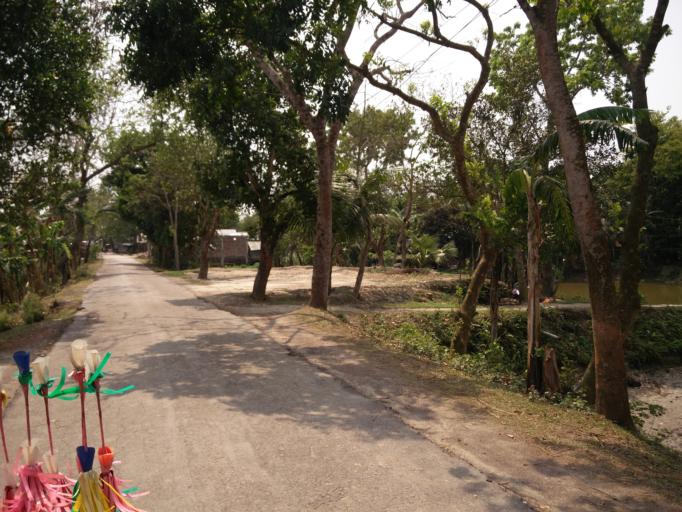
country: BD
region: Dhaka
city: Sherpur
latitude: 24.9470
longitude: 90.1606
